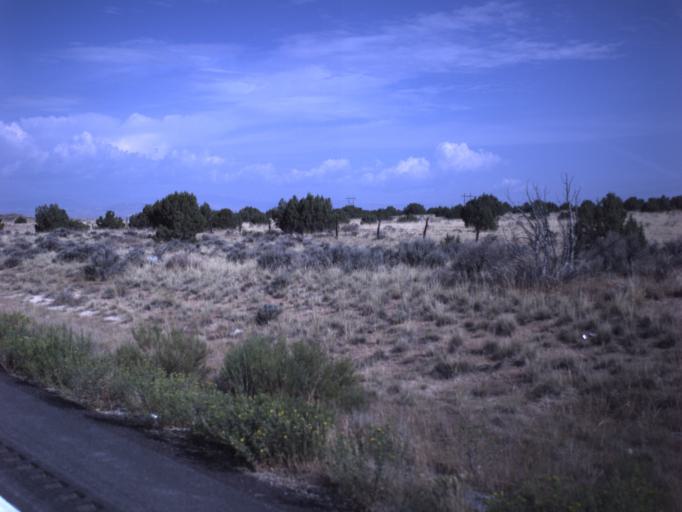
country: US
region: Utah
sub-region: Uintah County
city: Naples
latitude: 40.3255
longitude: -109.2680
